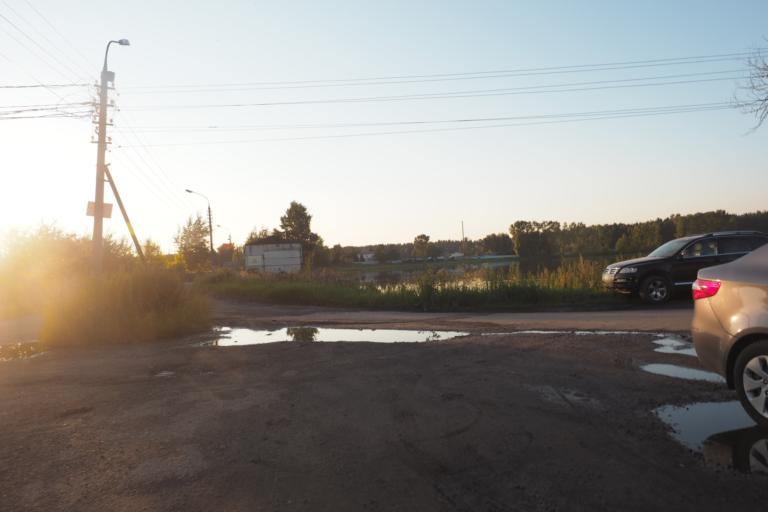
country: RU
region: Moskovskaya
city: Malyshevo
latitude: 55.5542
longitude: 38.3250
